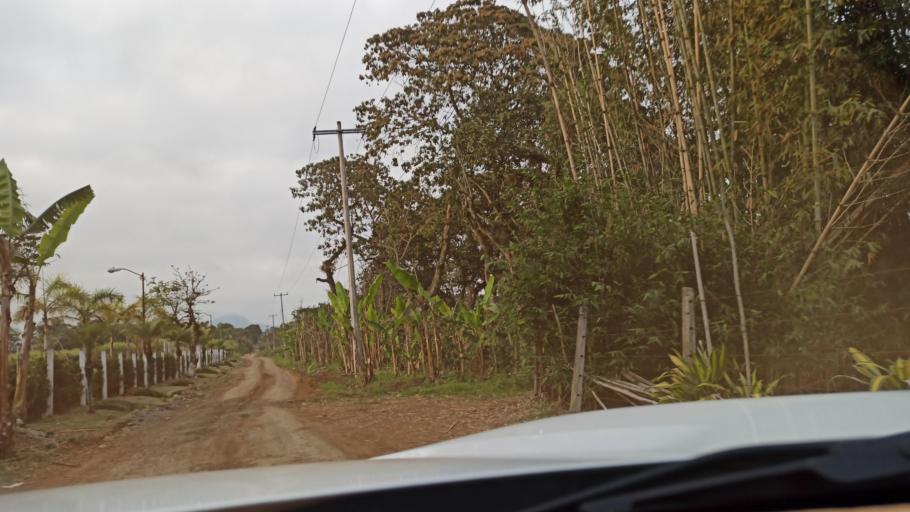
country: MX
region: Veracruz
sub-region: Fortin
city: Fortin de las Flores
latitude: 18.9199
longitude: -97.0039
